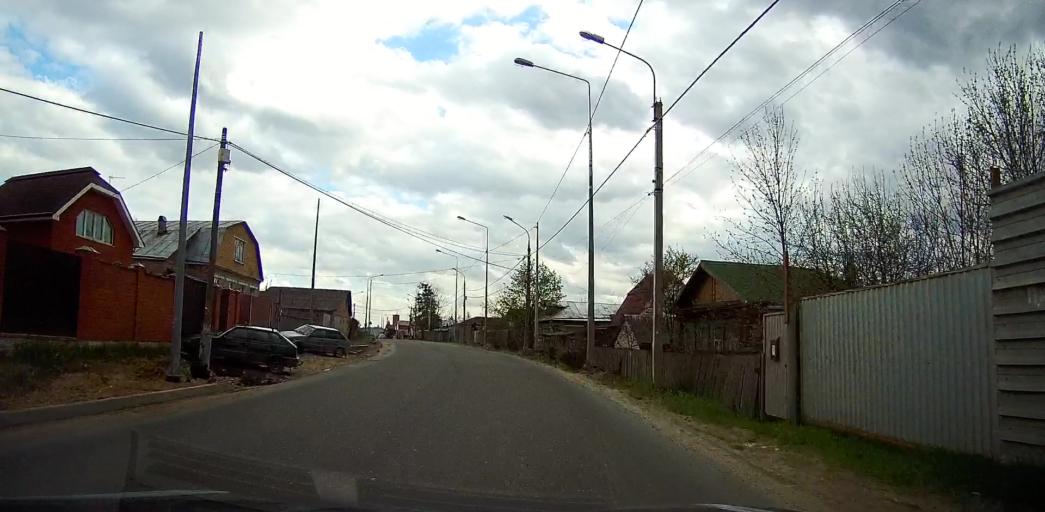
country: RU
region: Moskovskaya
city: Pavlovskiy Posad
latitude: 55.7908
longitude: 38.6849
